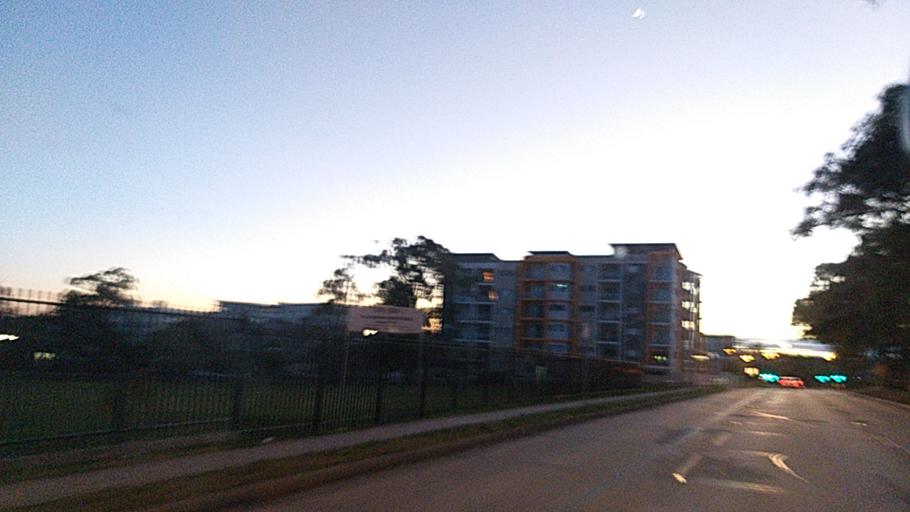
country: AU
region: New South Wales
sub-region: Campbelltown Municipality
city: Campbelltown
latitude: -34.0652
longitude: 150.8218
